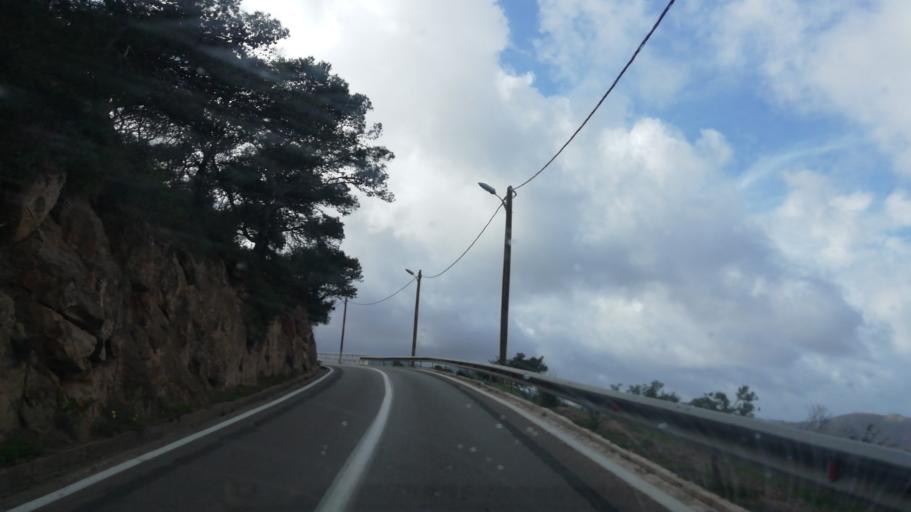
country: DZ
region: Oran
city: Oran
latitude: 35.7112
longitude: -0.6639
